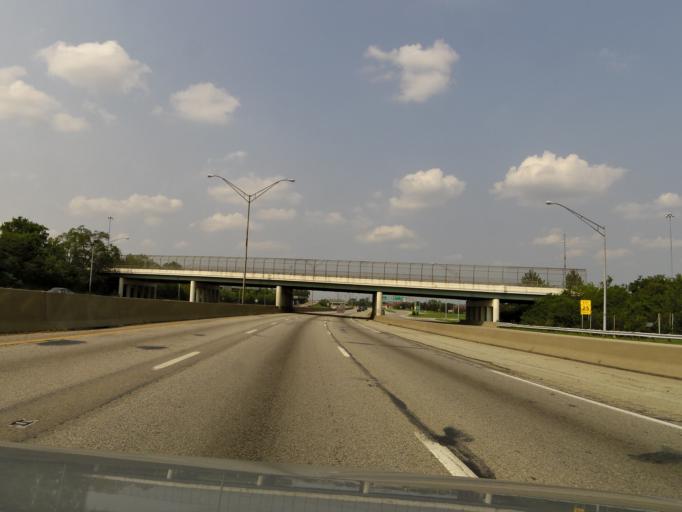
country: US
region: Ohio
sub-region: Hamilton County
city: Lincoln Heights
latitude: 39.2415
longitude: -84.4506
